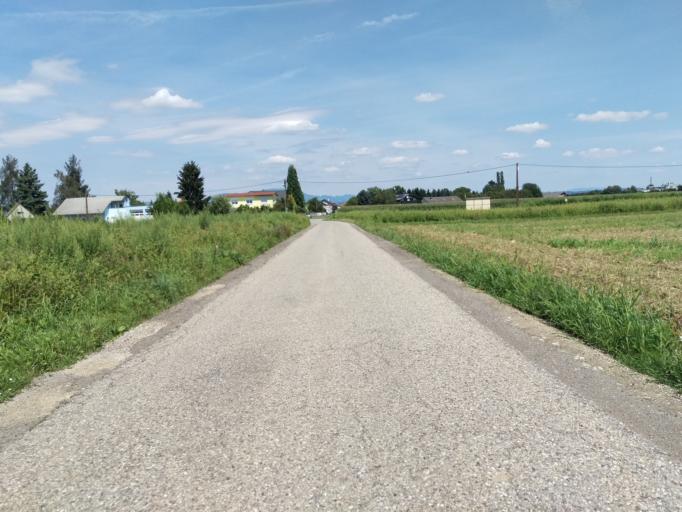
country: AT
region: Styria
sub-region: Politischer Bezirk Graz-Umgebung
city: Kalsdorf bei Graz
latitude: 46.9775
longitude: 15.4486
